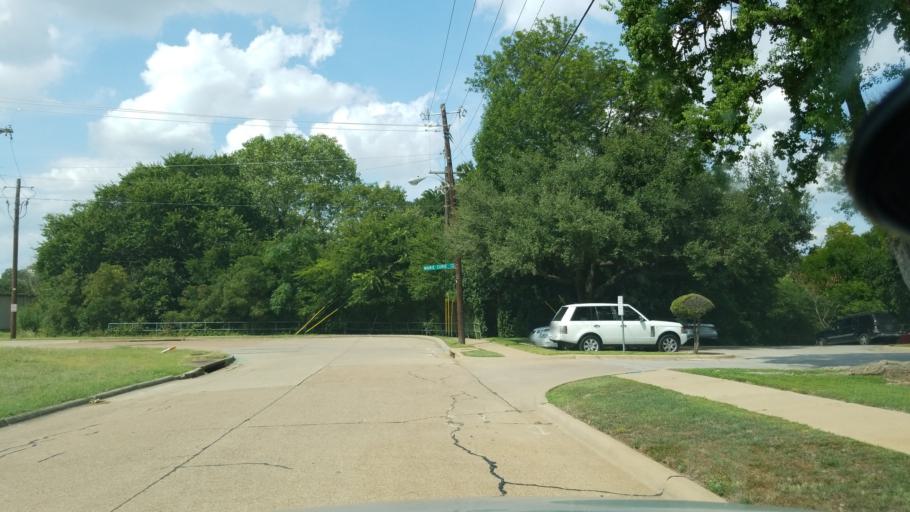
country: US
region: Texas
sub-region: Dallas County
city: Garland
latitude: 32.9182
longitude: -96.6589
